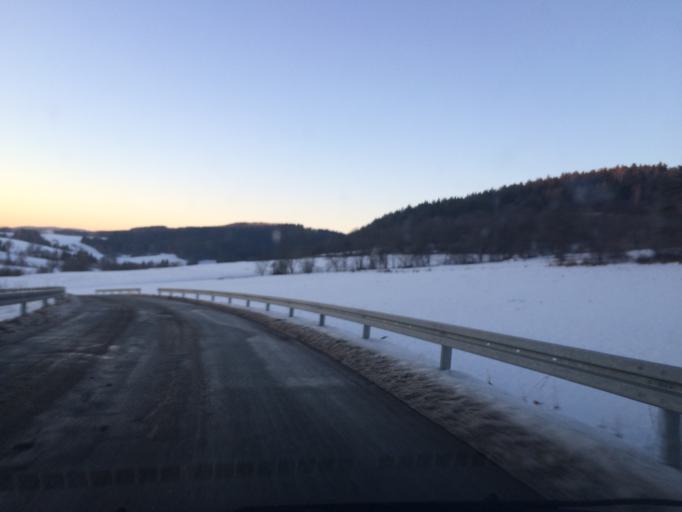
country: PL
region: Subcarpathian Voivodeship
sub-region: Powiat bieszczadzki
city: Ustrzyki Dolne
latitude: 49.3890
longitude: 22.6333
